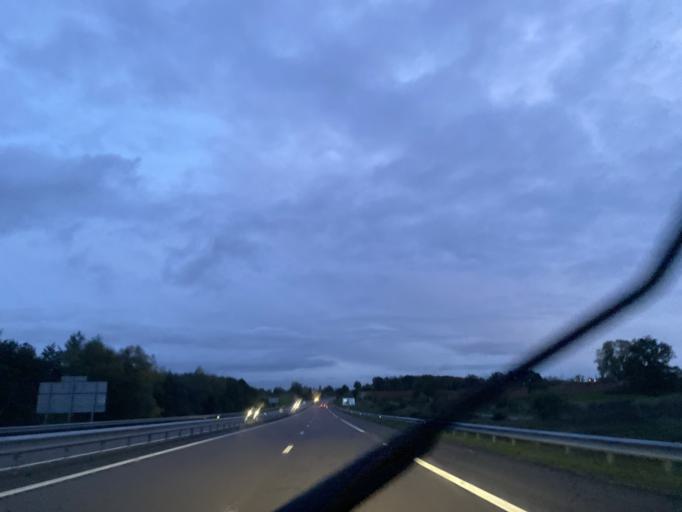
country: FR
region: Auvergne
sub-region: Departement de l'Allier
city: Estivareilles
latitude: 46.4058
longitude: 2.7101
